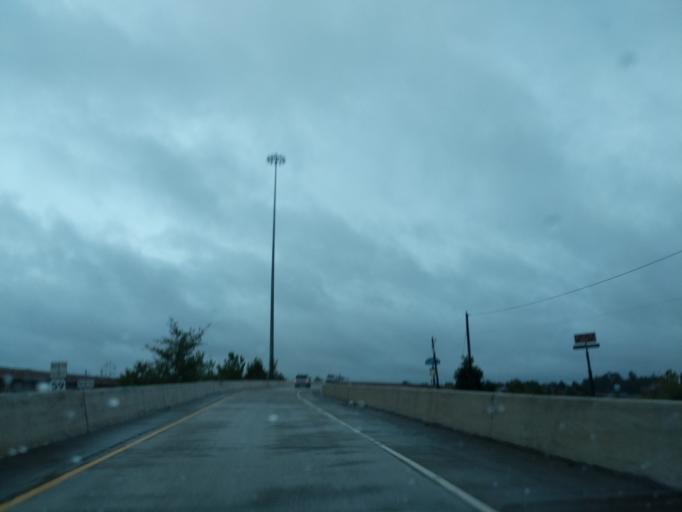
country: US
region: Texas
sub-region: Angelina County
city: Lufkin
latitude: 31.3081
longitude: -94.7262
